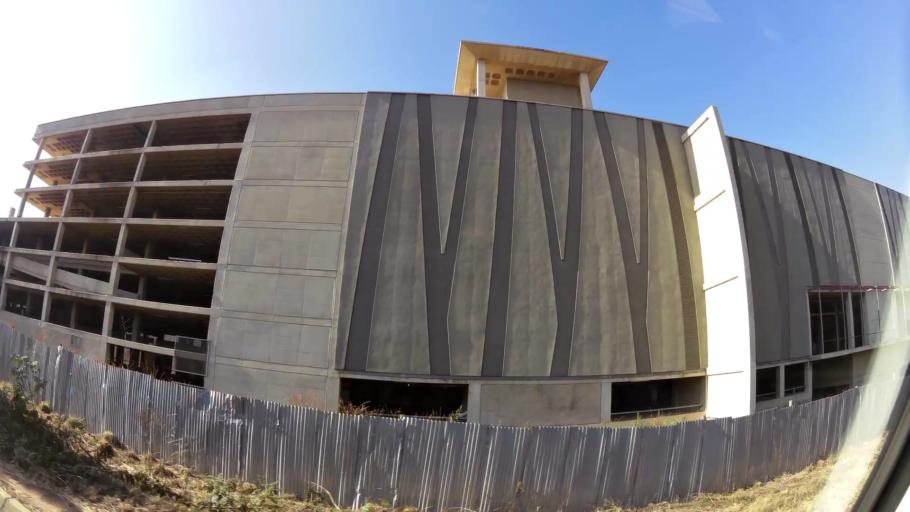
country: ZA
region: Gauteng
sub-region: City of Tshwane Metropolitan Municipality
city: Centurion
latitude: -25.8419
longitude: 28.2733
